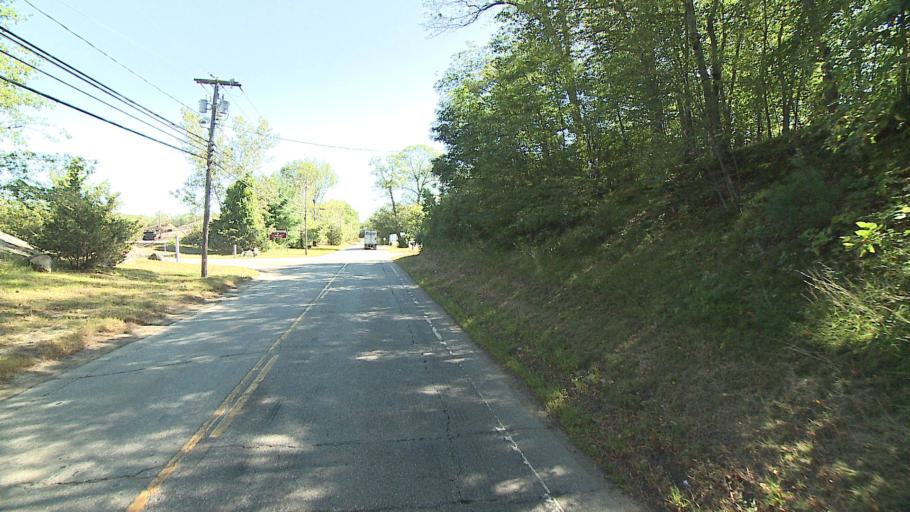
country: US
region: Connecticut
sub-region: New London County
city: Jewett City
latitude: 41.6245
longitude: -71.9719
